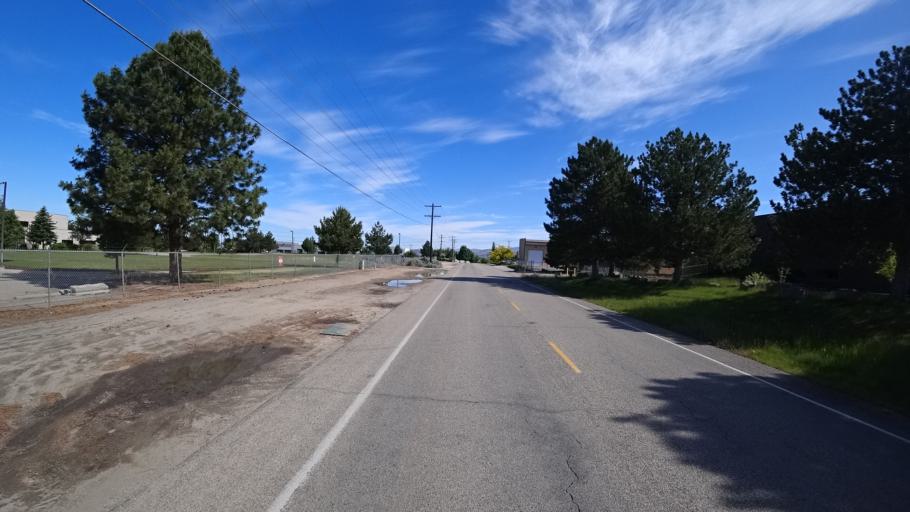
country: US
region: Idaho
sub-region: Ada County
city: Boise
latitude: 43.5665
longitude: -116.2074
